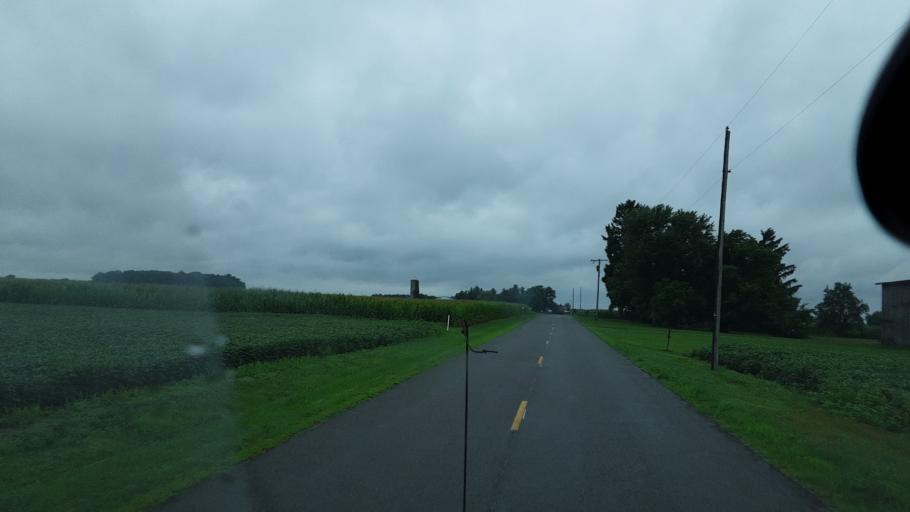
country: US
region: Ohio
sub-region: Van Wert County
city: Convoy
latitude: 40.8095
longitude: -84.6801
